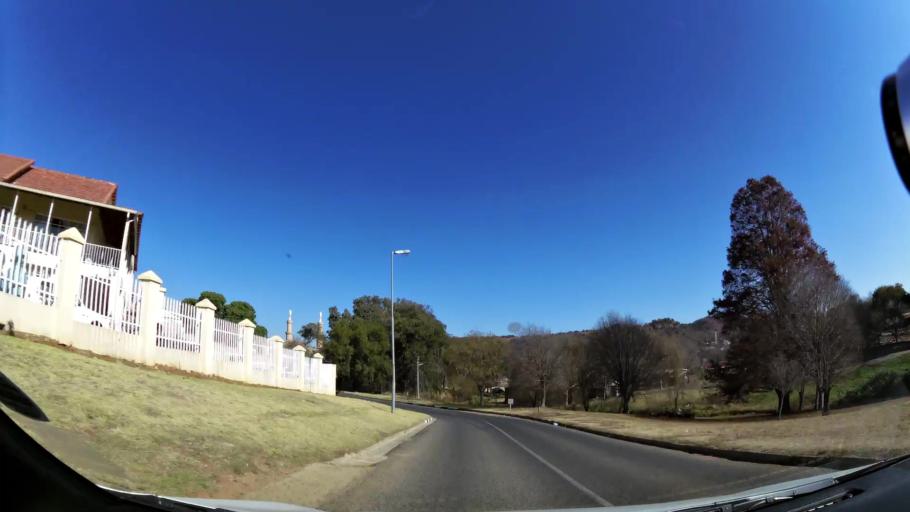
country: ZA
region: Gauteng
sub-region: City of Johannesburg Metropolitan Municipality
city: Johannesburg
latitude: -26.2748
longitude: 28.0092
